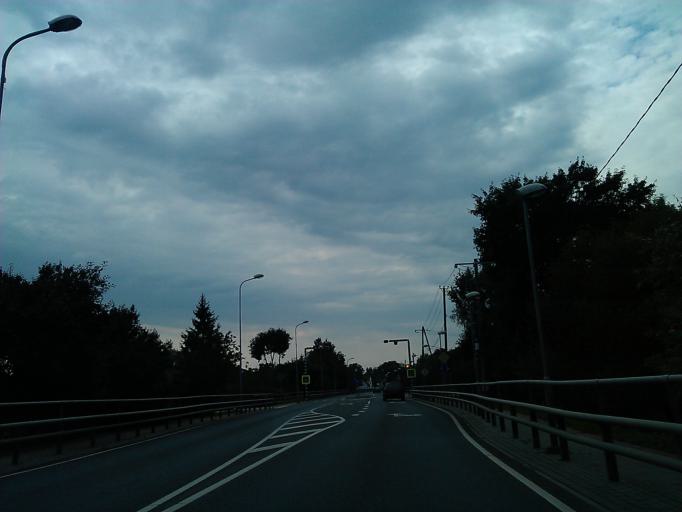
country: LV
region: Lecava
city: Iecava
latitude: 56.6007
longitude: 24.2022
